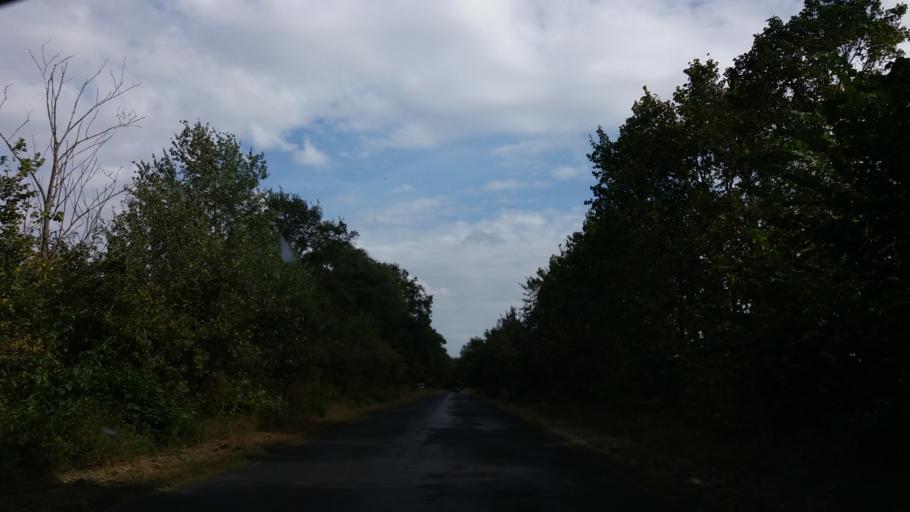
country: PL
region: West Pomeranian Voivodeship
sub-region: Powiat stargardzki
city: Dolice
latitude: 53.2492
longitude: 15.2120
